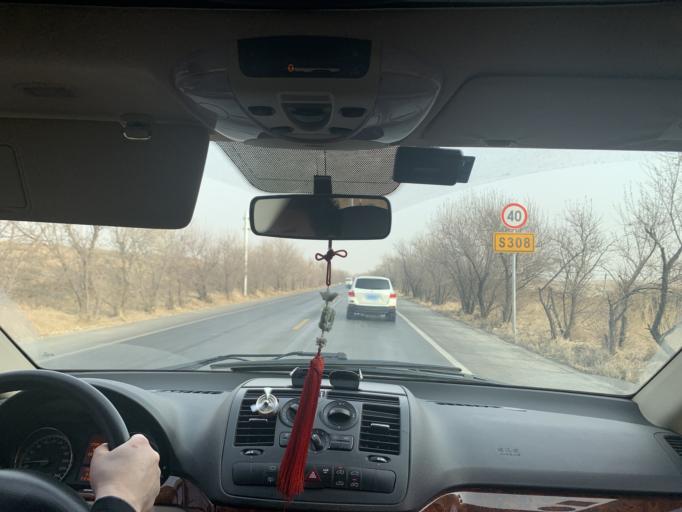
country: CN
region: Gansu Sheng
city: Gulang
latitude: 37.5532
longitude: 103.3516
